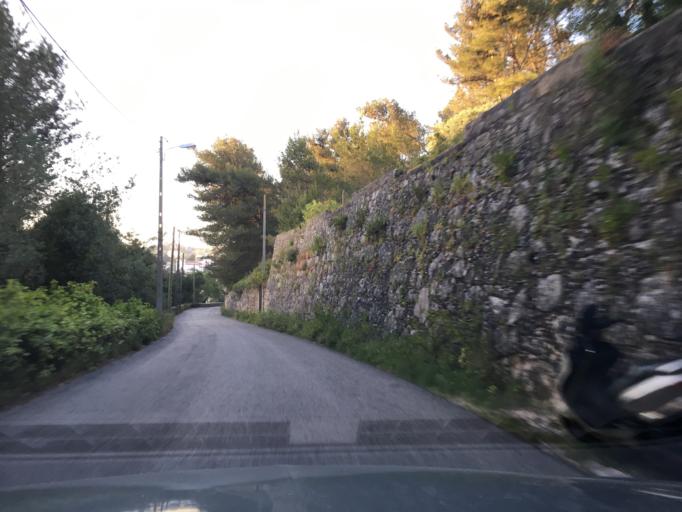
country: PT
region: Lisbon
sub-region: Oeiras
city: Barcarena
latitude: 38.7246
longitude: -9.2762
